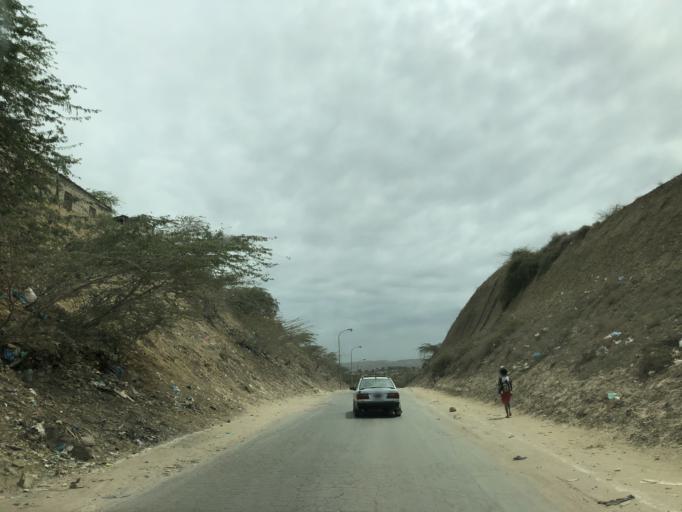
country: AO
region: Cuanza Sul
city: Sumbe
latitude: -11.2247
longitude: 13.8455
